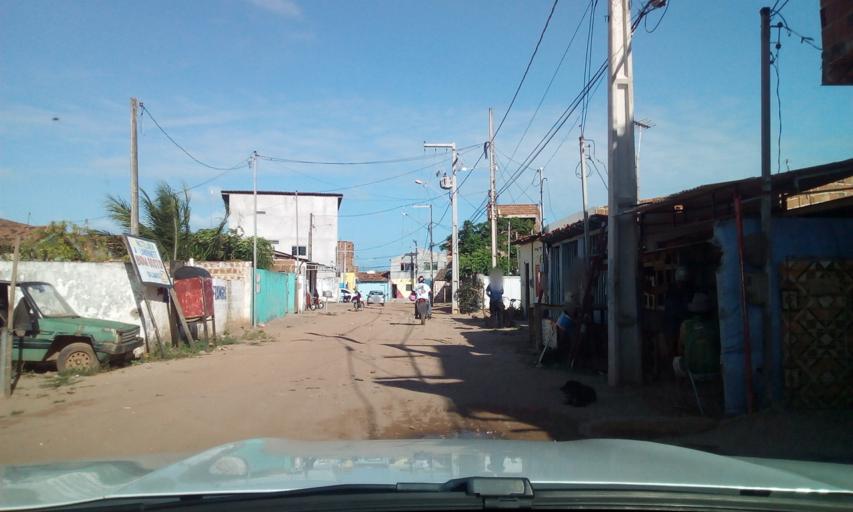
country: BR
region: Paraiba
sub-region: Cabedelo
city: Cabedelo
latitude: -7.0318
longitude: -34.8476
